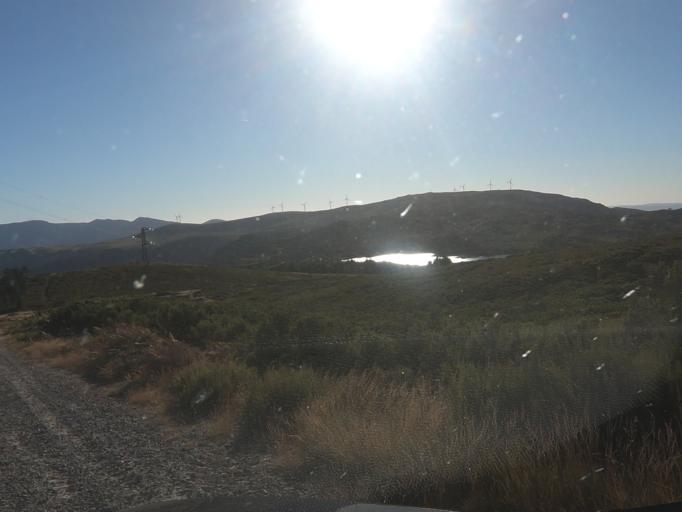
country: PT
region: Vila Real
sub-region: Vila Real
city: Vila Real
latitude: 41.3577
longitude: -7.7777
